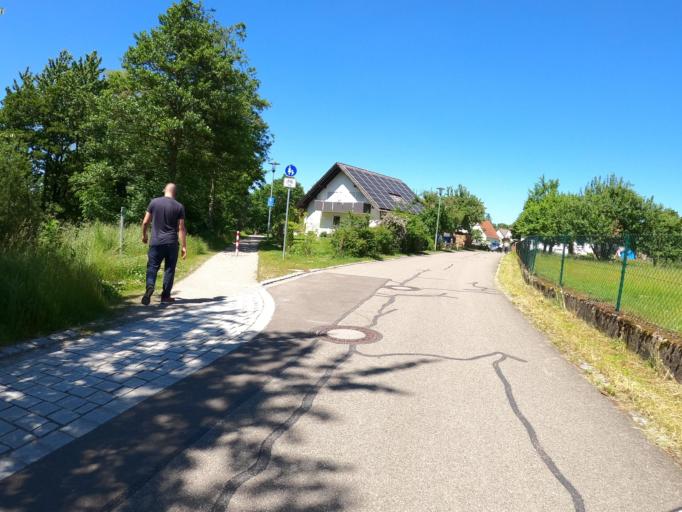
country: DE
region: Bavaria
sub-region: Swabia
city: Pfaffenhofen an der Roth
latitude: 48.3494
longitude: 10.1575
